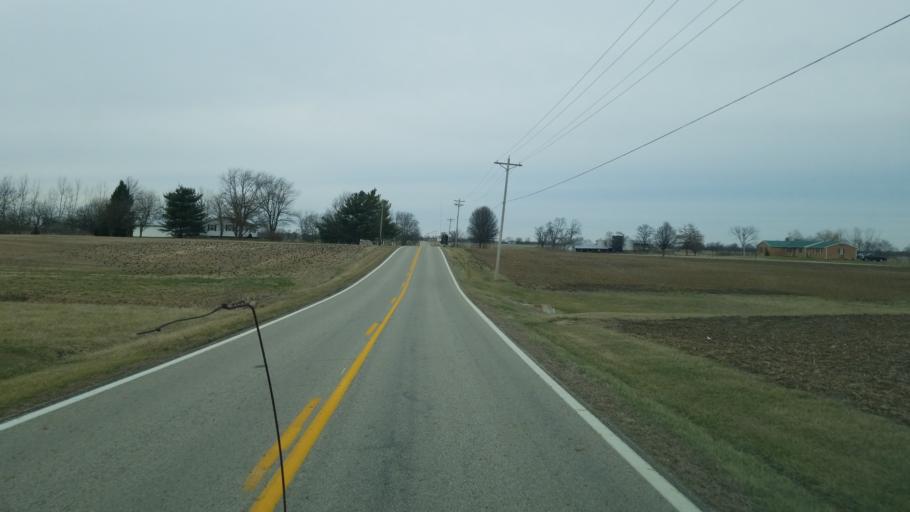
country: US
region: Ohio
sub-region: Pickaway County
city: Williamsport
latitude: 39.5365
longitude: -83.1235
